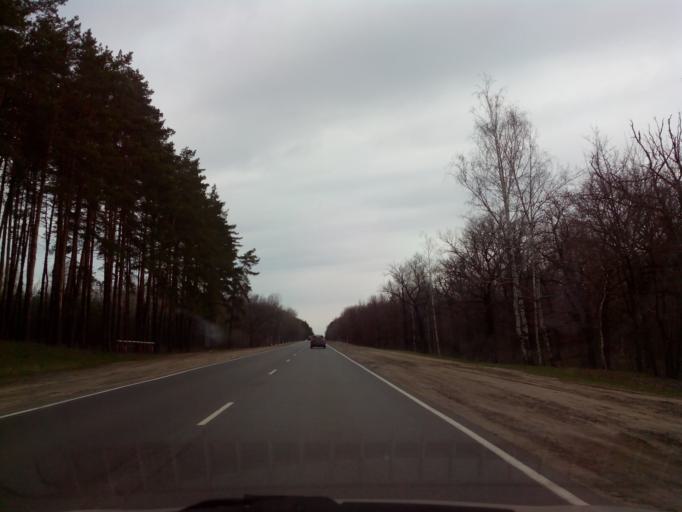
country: RU
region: Tambov
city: Bokino
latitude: 52.5409
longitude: 41.3553
